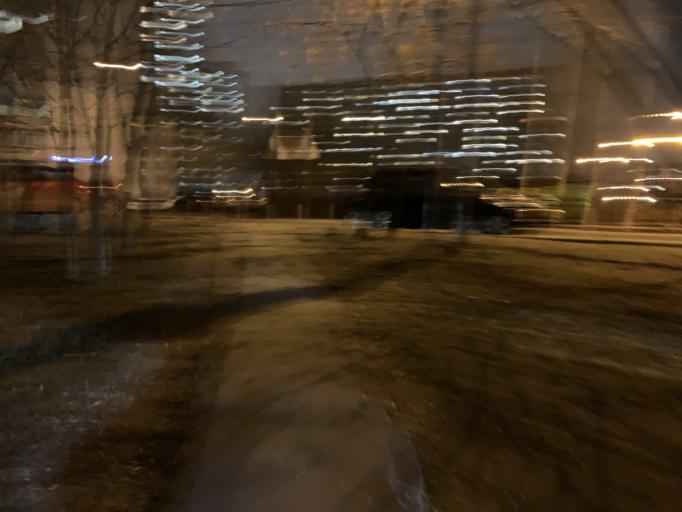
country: RU
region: Moskovskaya
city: Vostochnoe Degunino
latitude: 55.8779
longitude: 37.5610
